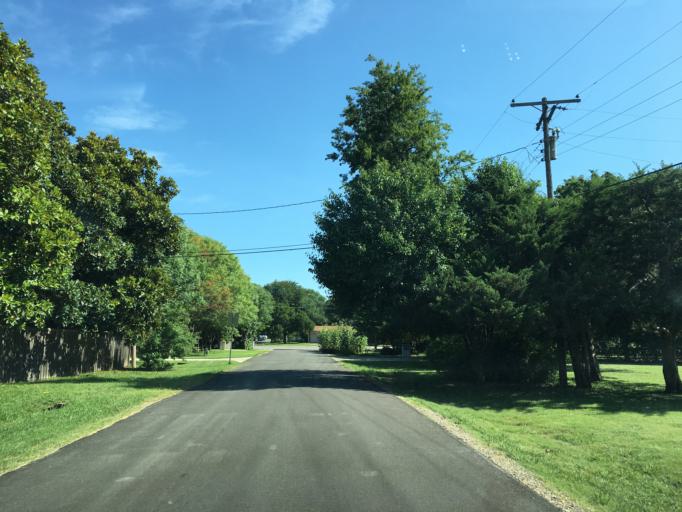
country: US
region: Texas
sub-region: Dallas County
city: Farmers Branch
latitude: 32.9233
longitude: -96.8692
